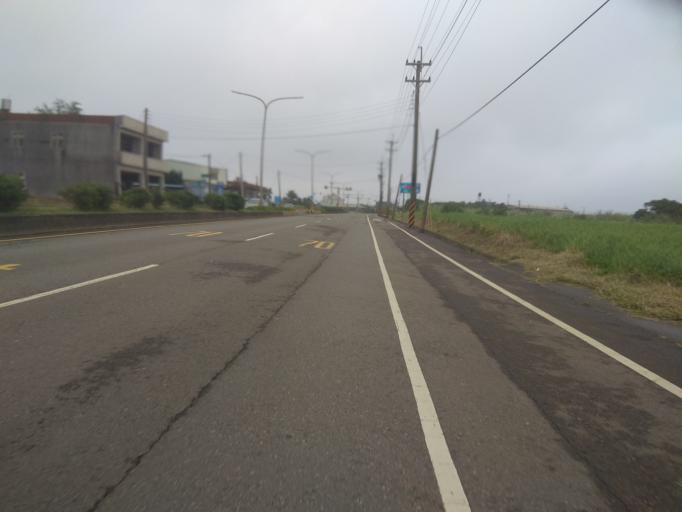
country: TW
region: Taiwan
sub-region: Hsinchu
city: Zhubei
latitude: 24.9931
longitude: 121.0341
